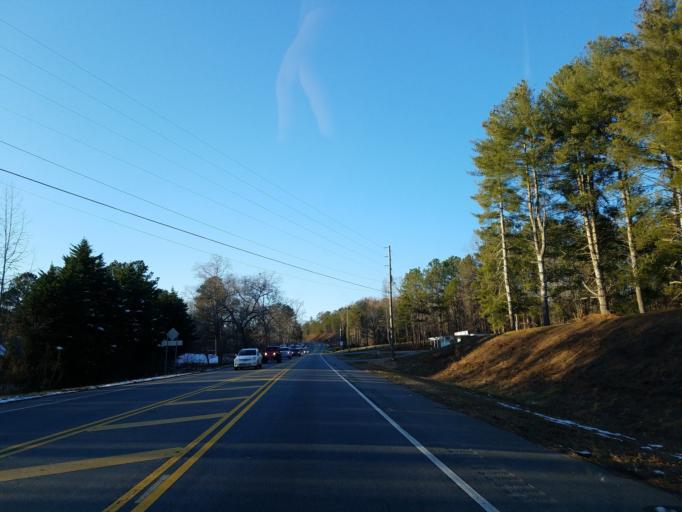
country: US
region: Georgia
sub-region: Dawson County
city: Dawsonville
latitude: 34.3873
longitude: -84.0778
